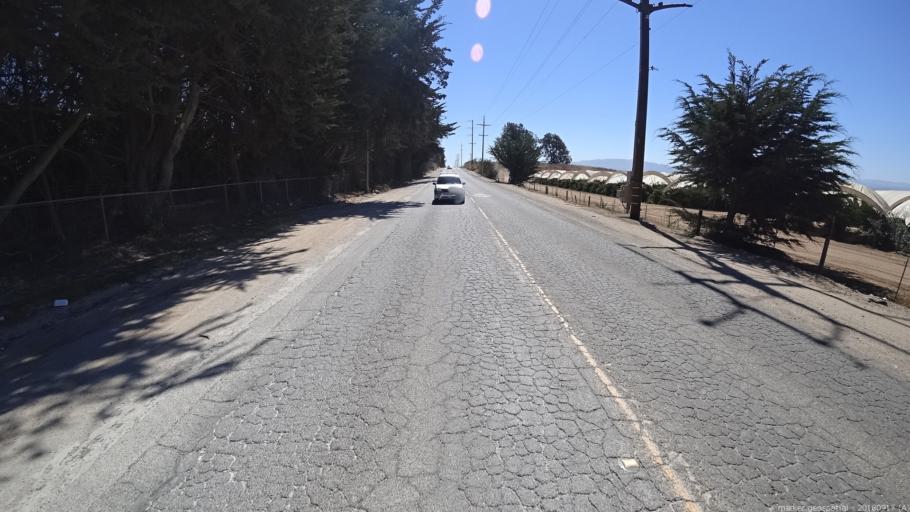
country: US
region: California
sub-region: Monterey County
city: Prunedale
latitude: 36.7500
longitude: -121.6070
